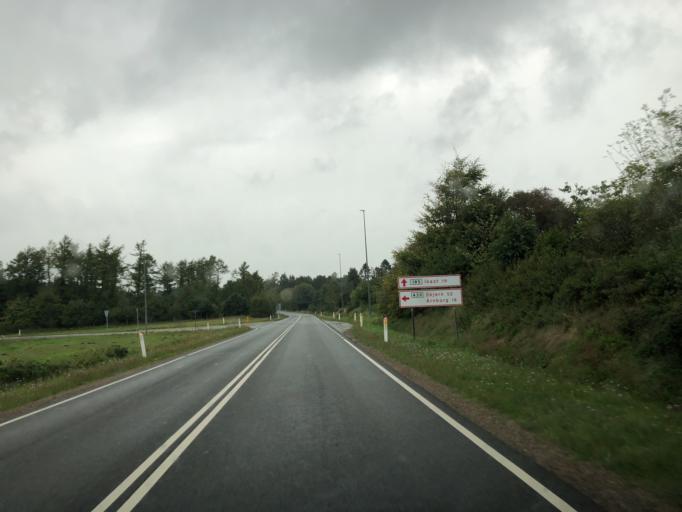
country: DK
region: South Denmark
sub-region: Vejle Kommune
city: Give
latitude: 55.9832
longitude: 9.2795
